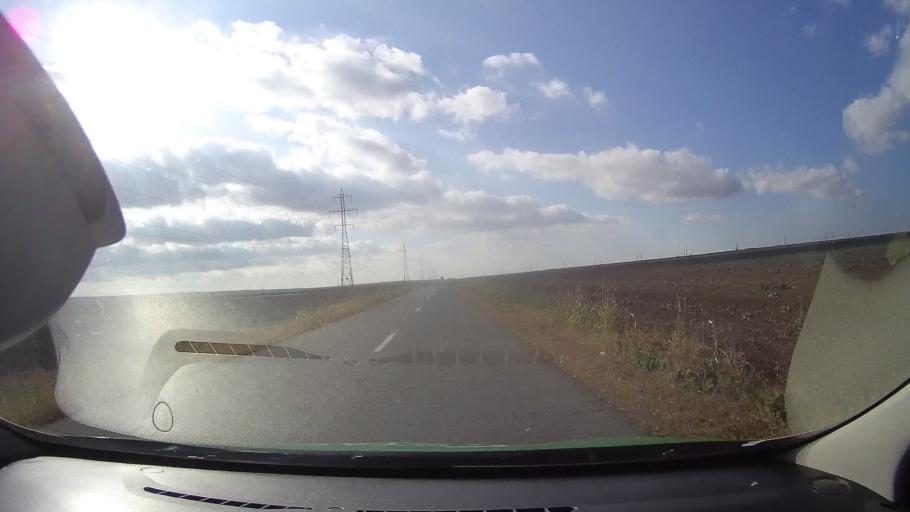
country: RO
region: Constanta
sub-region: Comuna Sacele
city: Sacele
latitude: 44.5094
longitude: 28.6757
